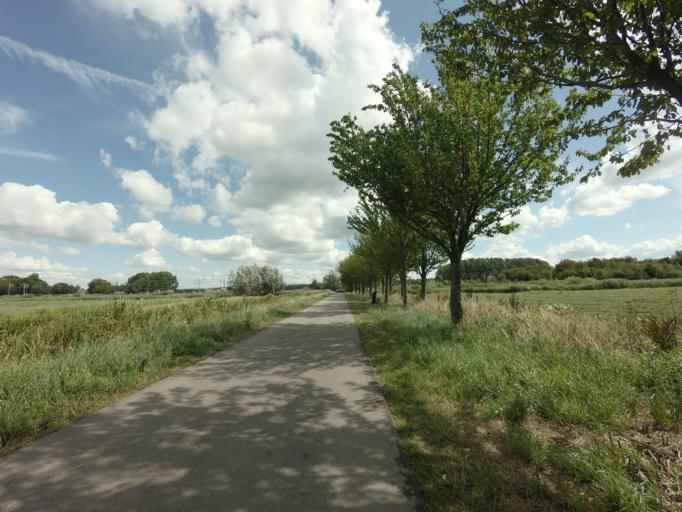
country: NL
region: Utrecht
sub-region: Stichtse Vecht
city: Vreeland
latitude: 52.2501
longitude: 4.9993
